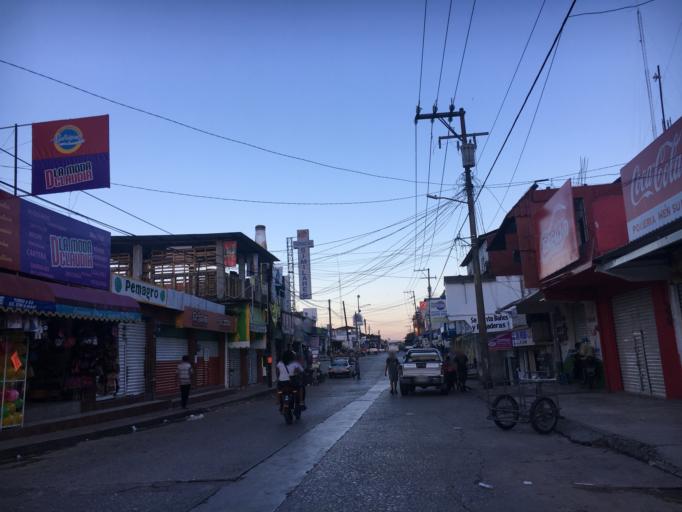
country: MX
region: Chiapas
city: Palenque
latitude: 17.5116
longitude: -91.9876
